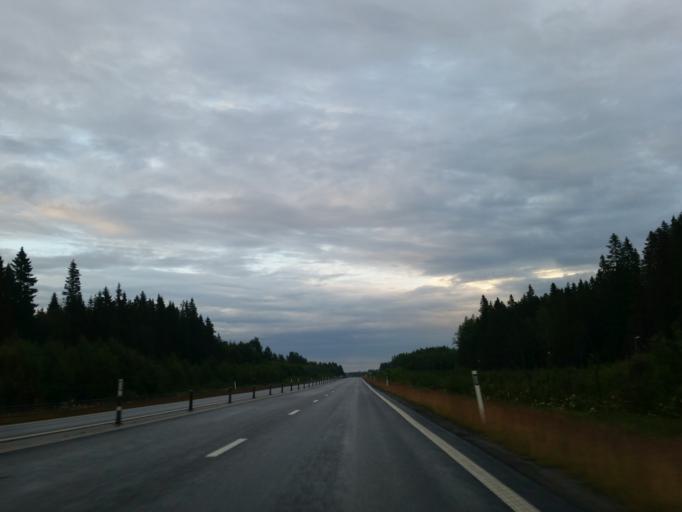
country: SE
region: Vaesterbotten
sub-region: Umea Kommun
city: Ersmark
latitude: 63.8492
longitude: 20.3563
